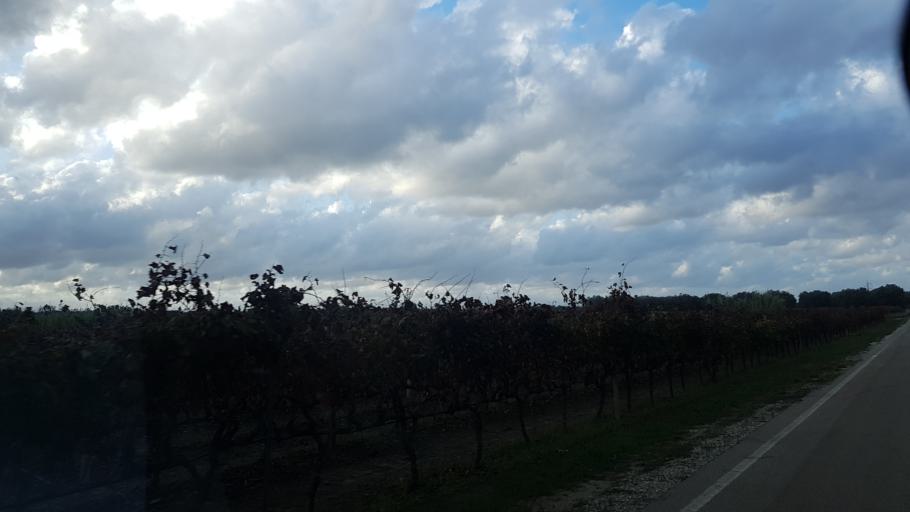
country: IT
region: Apulia
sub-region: Provincia di Brindisi
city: San Pietro Vernotico
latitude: 40.5097
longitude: 18.0202
